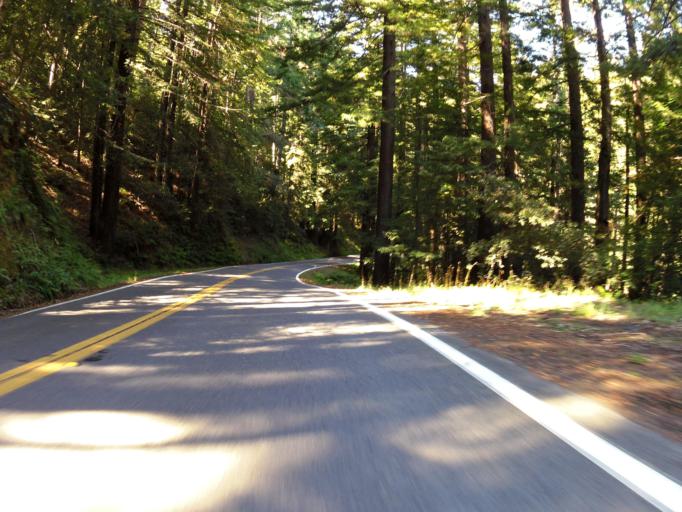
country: US
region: California
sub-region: Mendocino County
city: Fort Bragg
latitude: 39.7224
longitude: -123.8051
